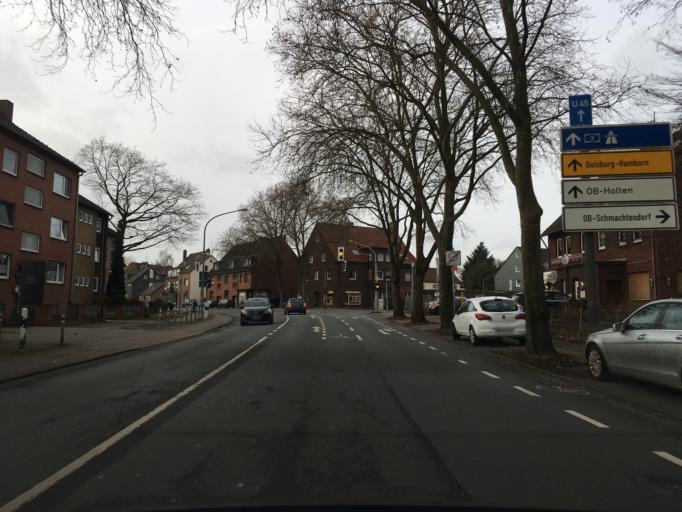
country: DE
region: North Rhine-Westphalia
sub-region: Regierungsbezirk Dusseldorf
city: Oberhausen
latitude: 51.5140
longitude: 6.8265
